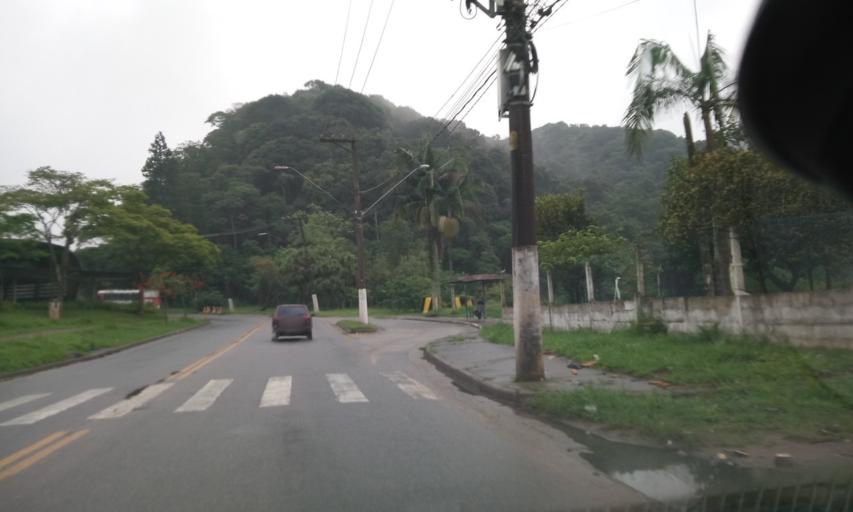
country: BR
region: Sao Paulo
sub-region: Maua
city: Maua
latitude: -23.7303
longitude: -46.4955
